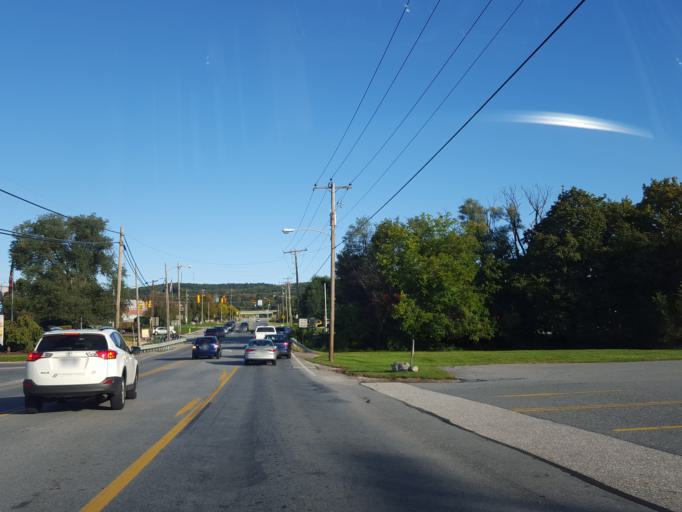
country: US
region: Pennsylvania
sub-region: York County
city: East York
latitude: 39.9779
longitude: -76.6812
